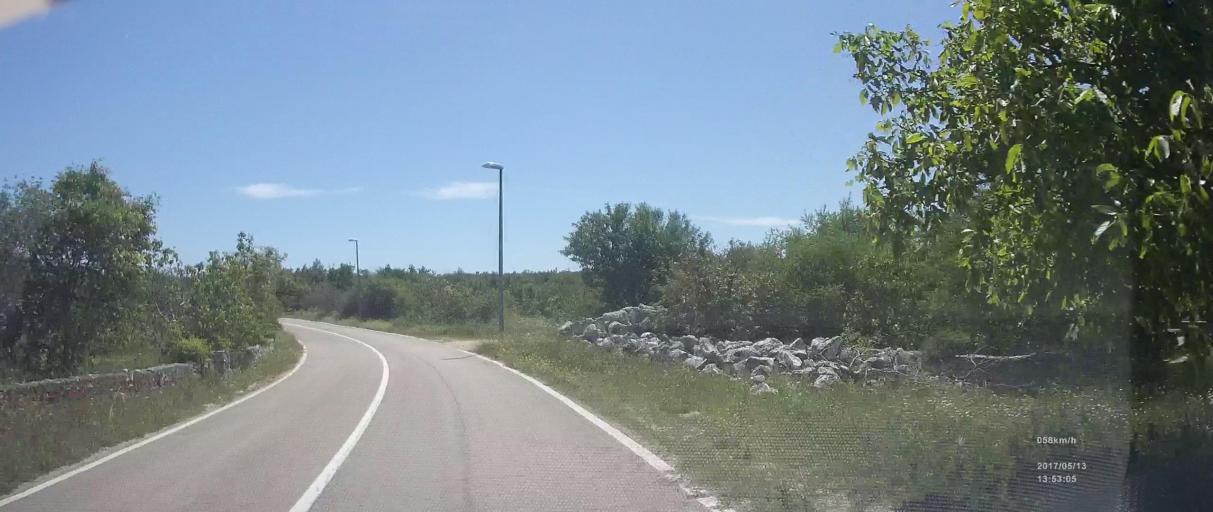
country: HR
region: Sibensko-Kniniska
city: Primosten
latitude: 43.6019
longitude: 15.9964
